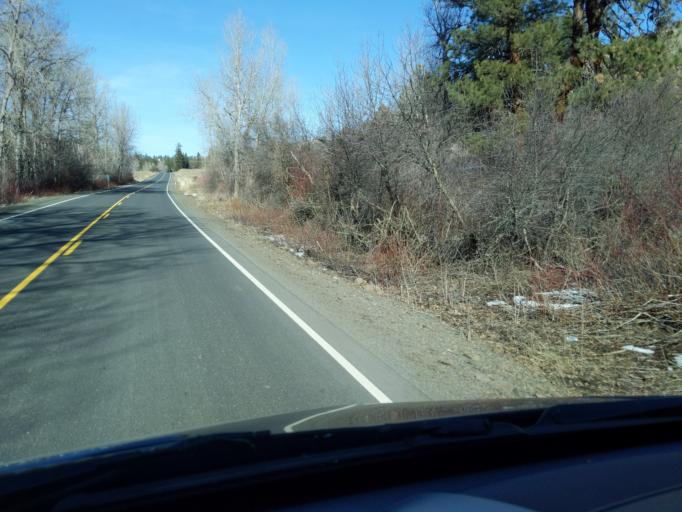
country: US
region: Oregon
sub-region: Grant County
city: John Day
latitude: 44.8542
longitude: -119.0298
